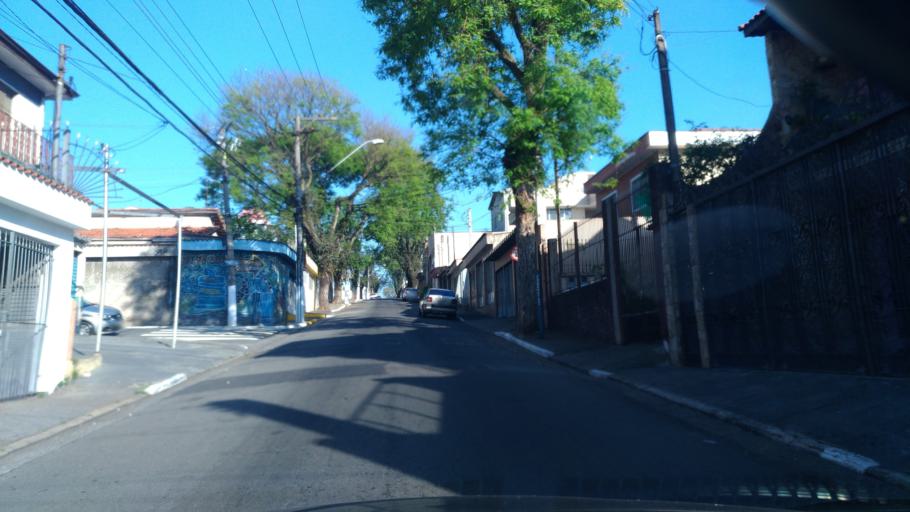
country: BR
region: Sao Paulo
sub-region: Sao Bernardo Do Campo
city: Sao Bernardo do Campo
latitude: -23.6691
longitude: -46.5900
